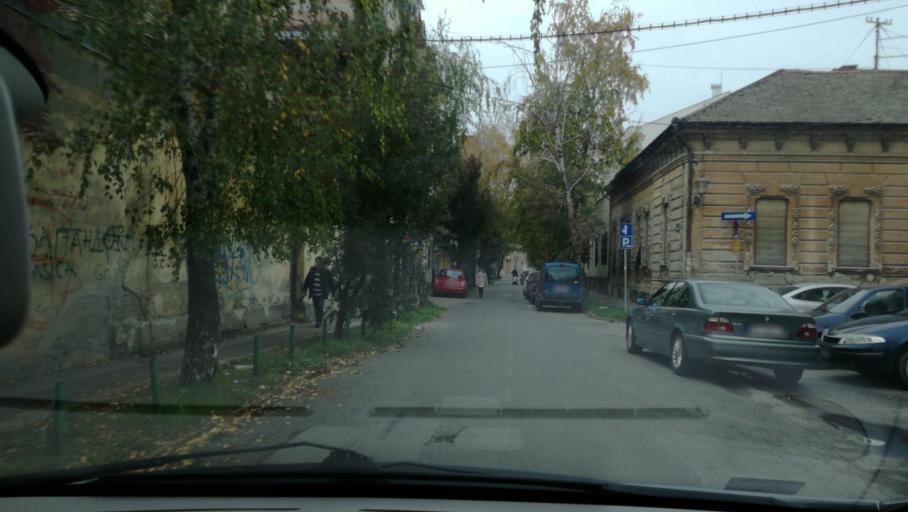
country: RS
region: Autonomna Pokrajina Vojvodina
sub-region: Juznobacki Okrug
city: Novi Sad
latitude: 45.2591
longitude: 19.8410
